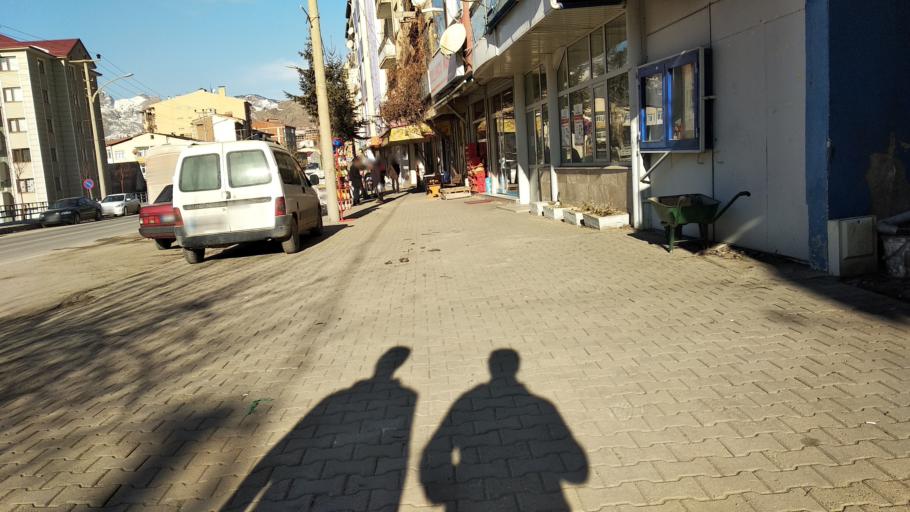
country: TR
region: Gumushane
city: Gumushkhane
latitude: 40.4547
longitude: 39.4922
